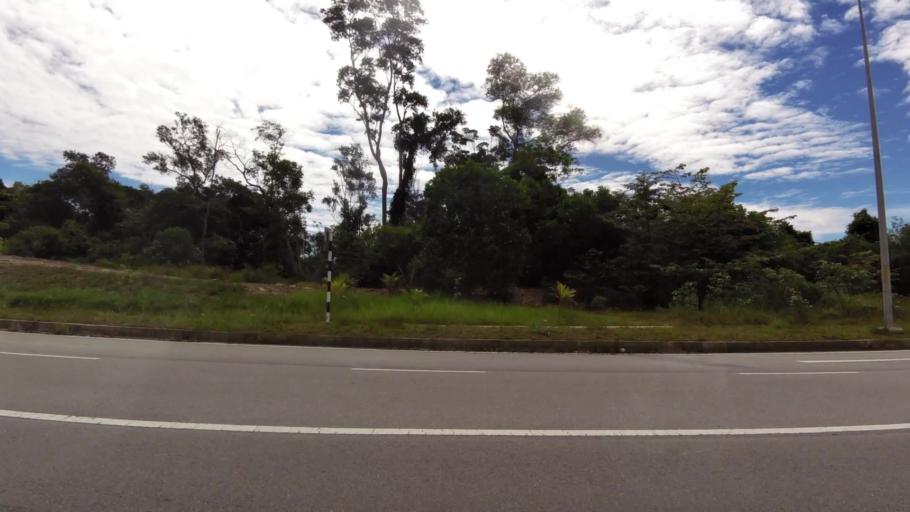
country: BN
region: Brunei and Muara
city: Bandar Seri Begawan
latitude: 4.9857
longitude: 115.0179
